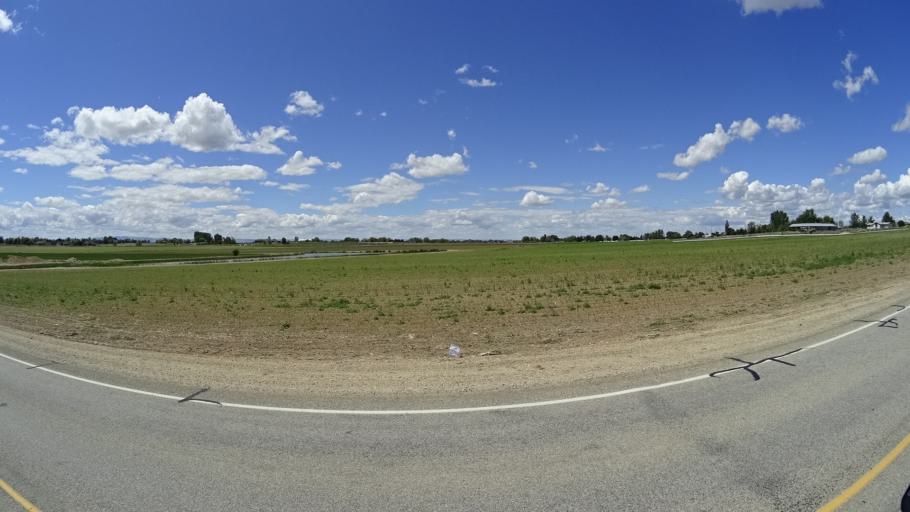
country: US
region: Idaho
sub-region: Ada County
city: Meridian
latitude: 43.5729
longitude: -116.4336
